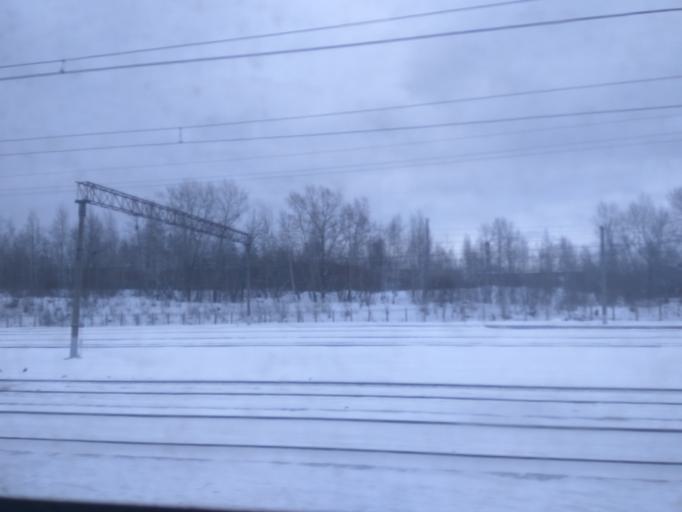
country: RU
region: Moscow
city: Annino
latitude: 55.5874
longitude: 37.6147
